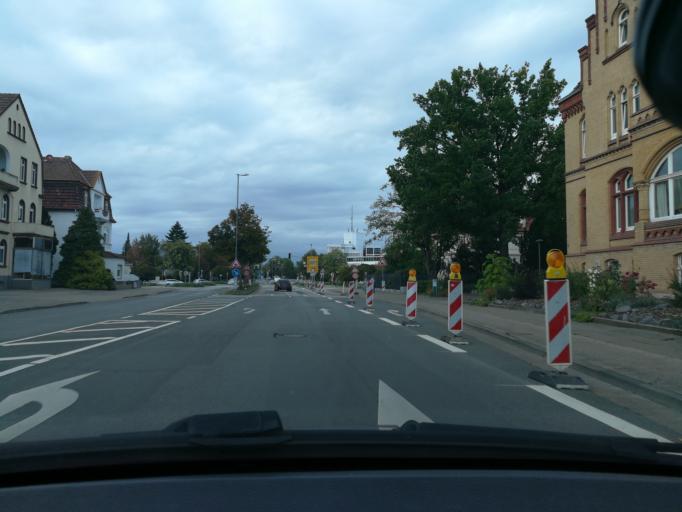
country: DE
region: North Rhine-Westphalia
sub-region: Regierungsbezirk Detmold
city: Minden
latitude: 52.2987
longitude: 8.9159
